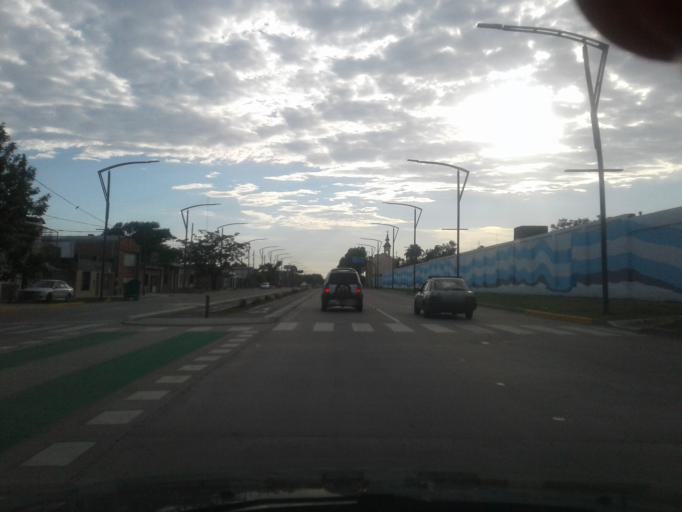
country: AR
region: Santa Fe
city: Perez
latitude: -32.9596
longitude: -60.7143
